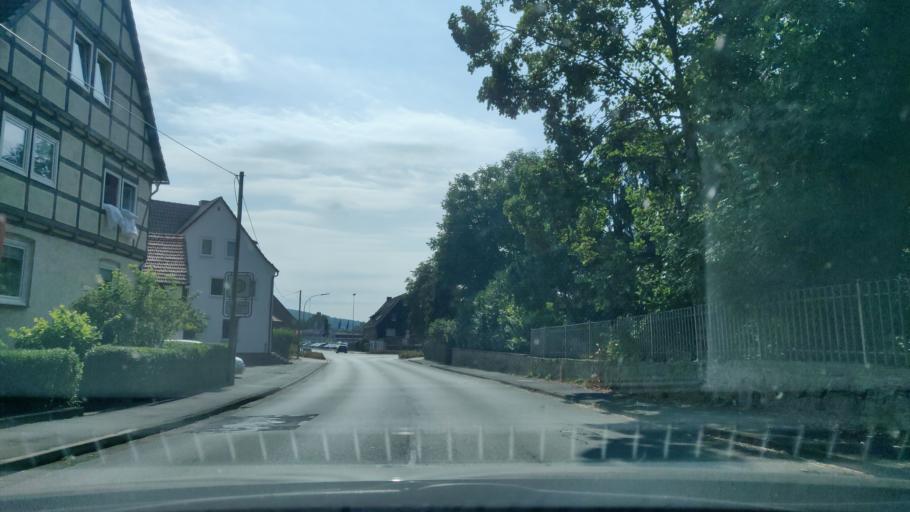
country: DE
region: Hesse
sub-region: Regierungsbezirk Kassel
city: Bad Wildungen
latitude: 51.1673
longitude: 9.1355
